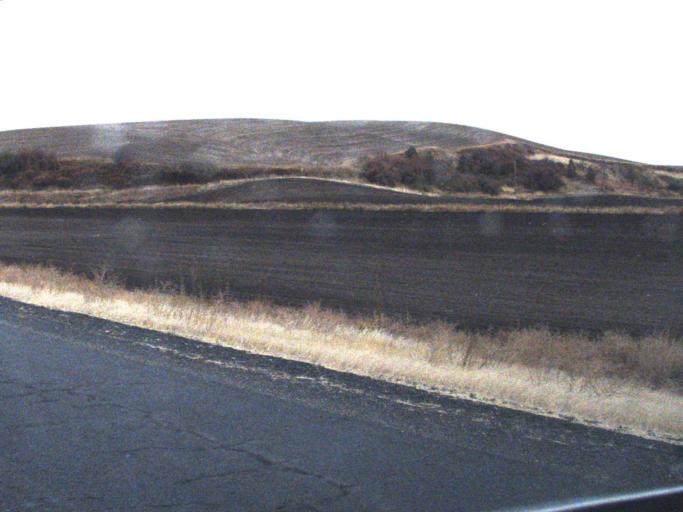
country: US
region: Washington
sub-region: Whitman County
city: Colfax
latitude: 46.9528
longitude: -117.3337
